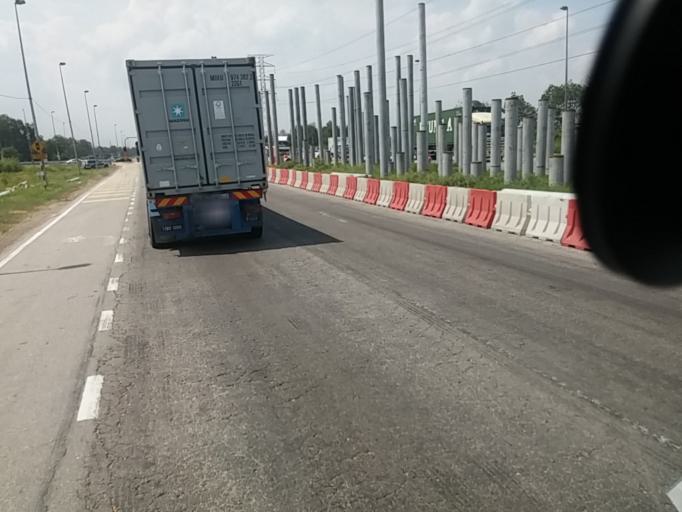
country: MY
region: Selangor
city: Klang
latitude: 2.9688
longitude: 101.3627
